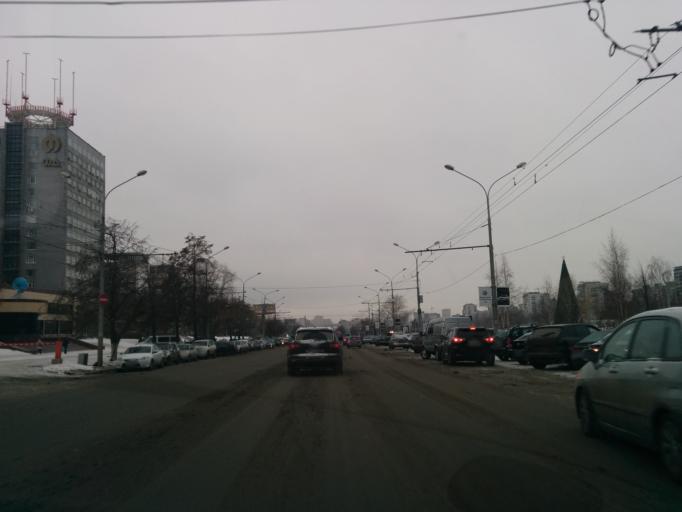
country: RU
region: Perm
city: Perm
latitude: 58.0101
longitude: 56.2328
